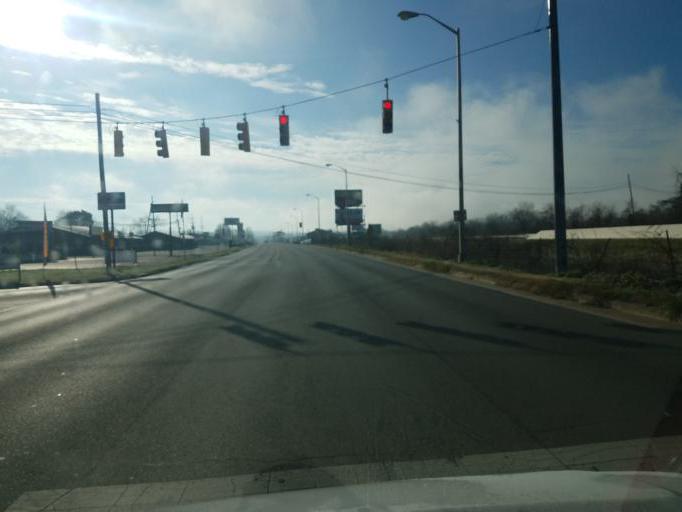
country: US
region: Ohio
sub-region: Scioto County
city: Wheelersburg
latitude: 38.7232
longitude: -82.8595
